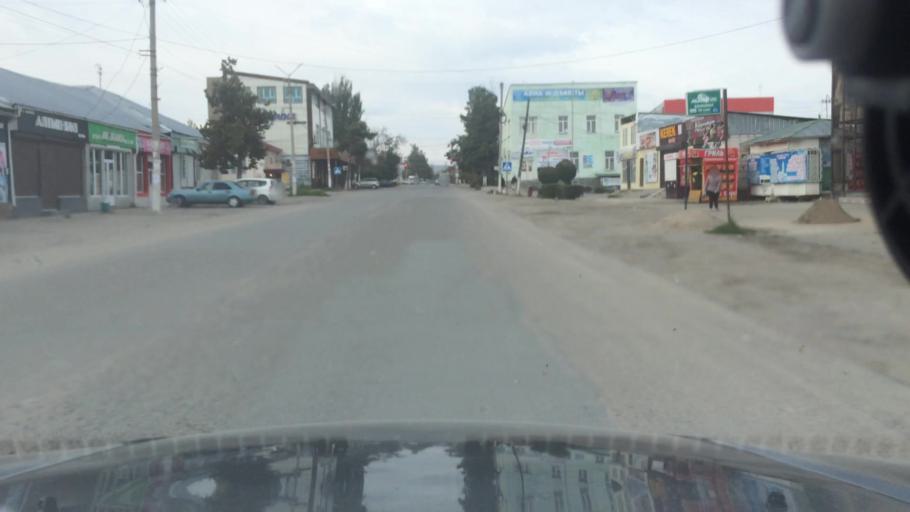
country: KG
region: Ysyk-Koel
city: Karakol
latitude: 42.4909
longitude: 78.3927
